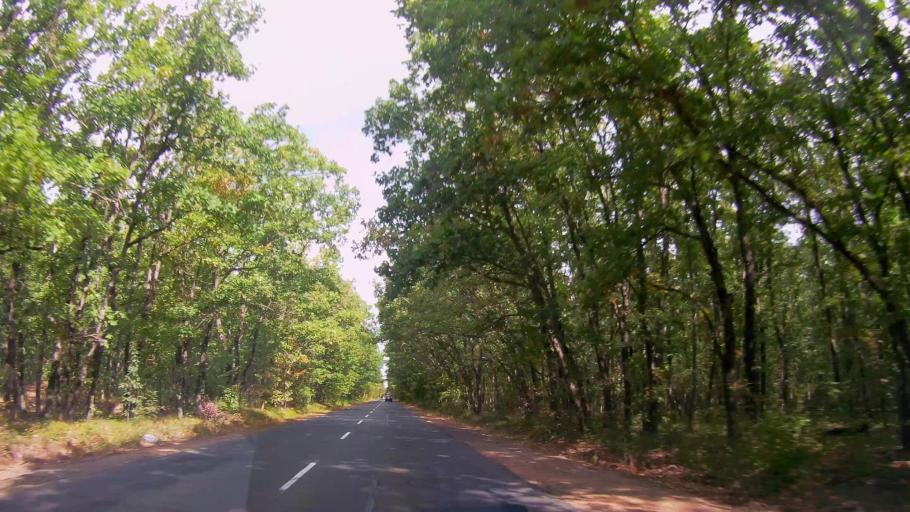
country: BG
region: Burgas
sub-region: Obshtina Primorsko
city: Primorsko
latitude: 42.2871
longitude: 27.7359
